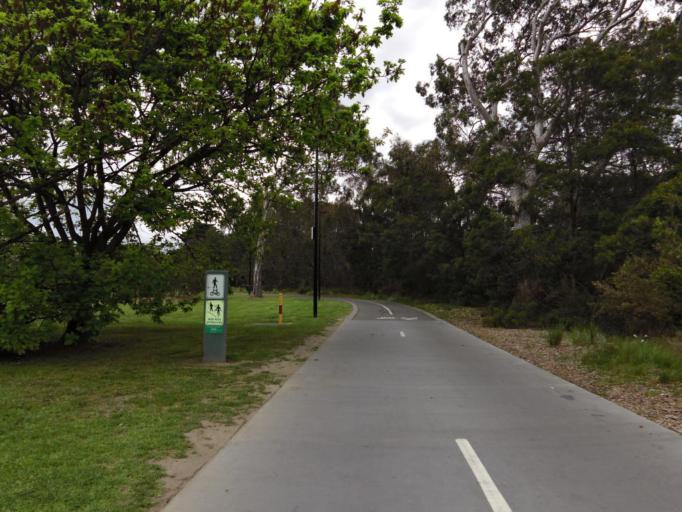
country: AU
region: Victoria
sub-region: Stonnington
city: Glen Iris
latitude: -37.8567
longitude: 145.0598
